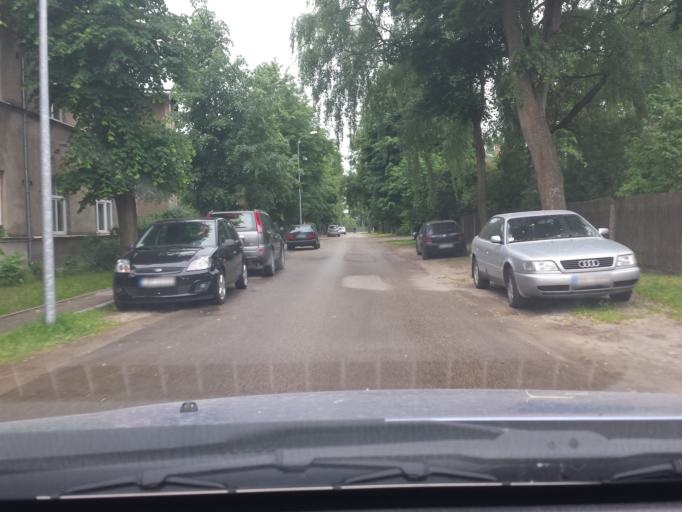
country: LV
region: Riga
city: Jaunciems
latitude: 56.9734
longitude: 24.1843
